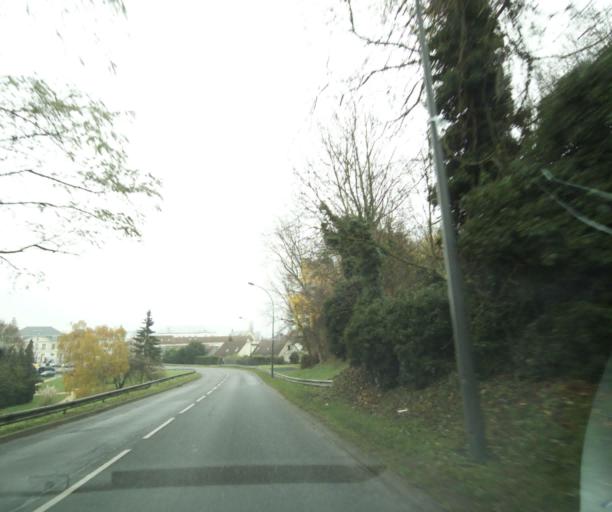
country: FR
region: Ile-de-France
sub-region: Departement de Seine-Saint-Denis
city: Vaujours
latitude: 48.9286
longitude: 2.5700
